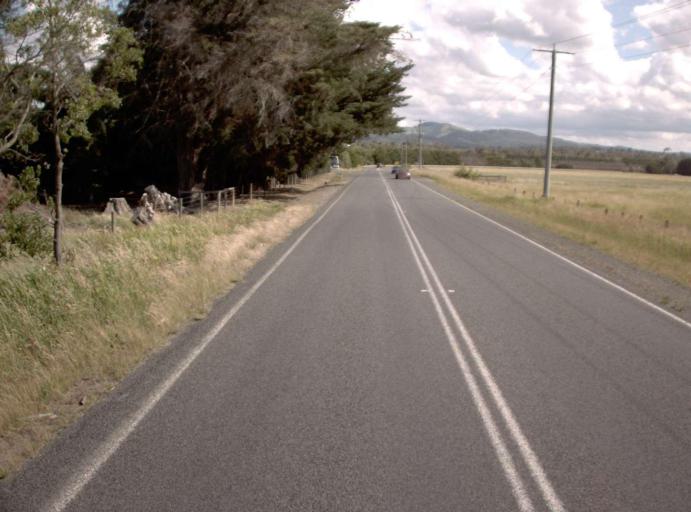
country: AU
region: Victoria
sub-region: Latrobe
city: Morwell
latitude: -38.2893
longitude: 146.4298
